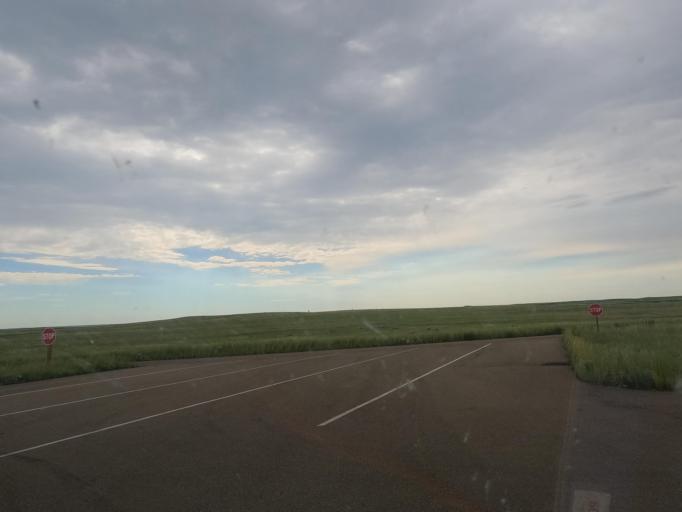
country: CA
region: Saskatchewan
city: Assiniboia
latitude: 49.0650
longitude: -106.5228
